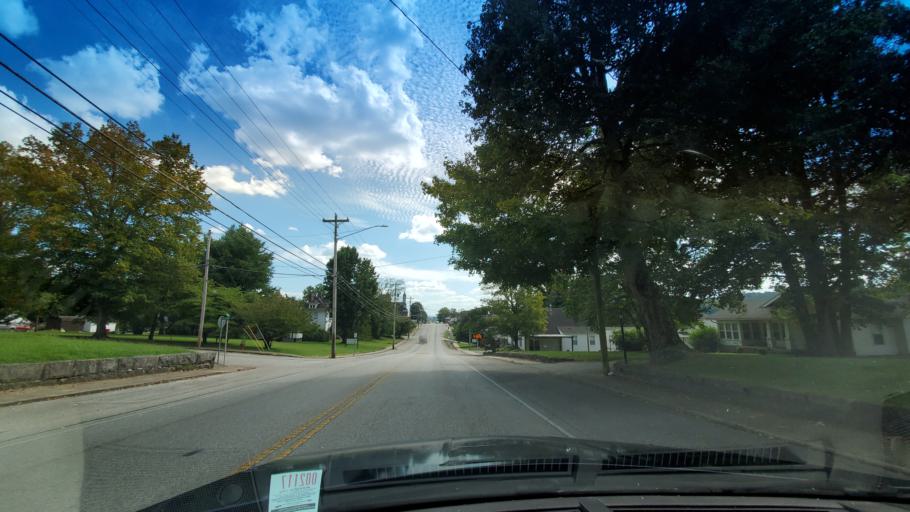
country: US
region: Tennessee
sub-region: Smith County
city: Carthage
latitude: 36.2573
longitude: -85.9512
